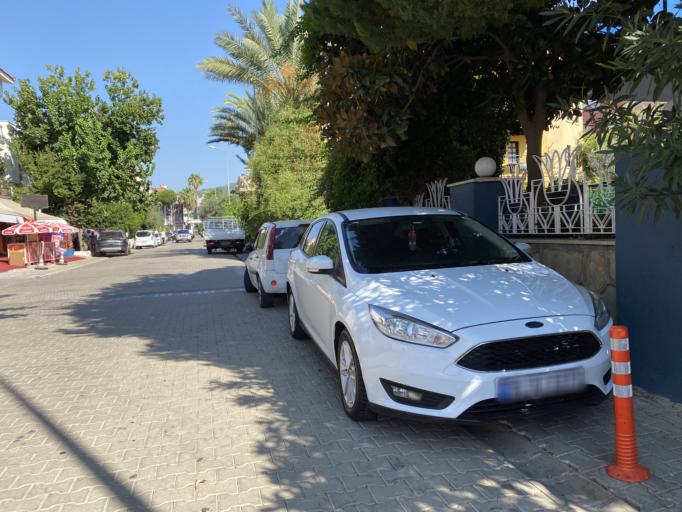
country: TR
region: Mugla
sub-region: Marmaris
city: Marmaris
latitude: 36.8442
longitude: 28.2528
